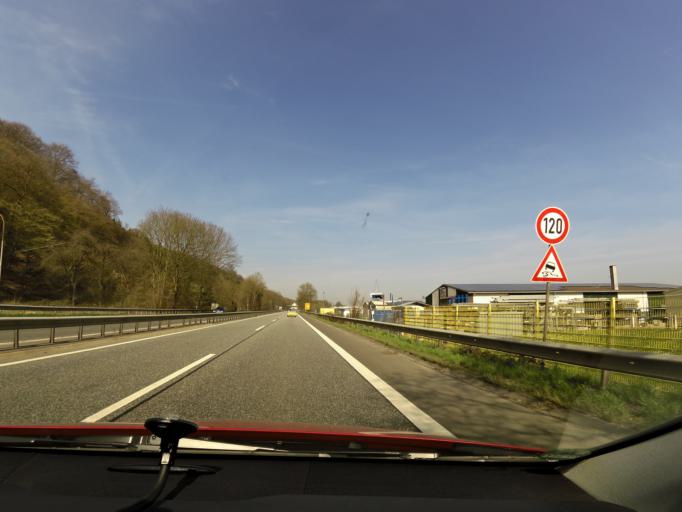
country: DE
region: Rheinland-Pfalz
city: Bad Breisig
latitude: 50.5301
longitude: 7.2739
